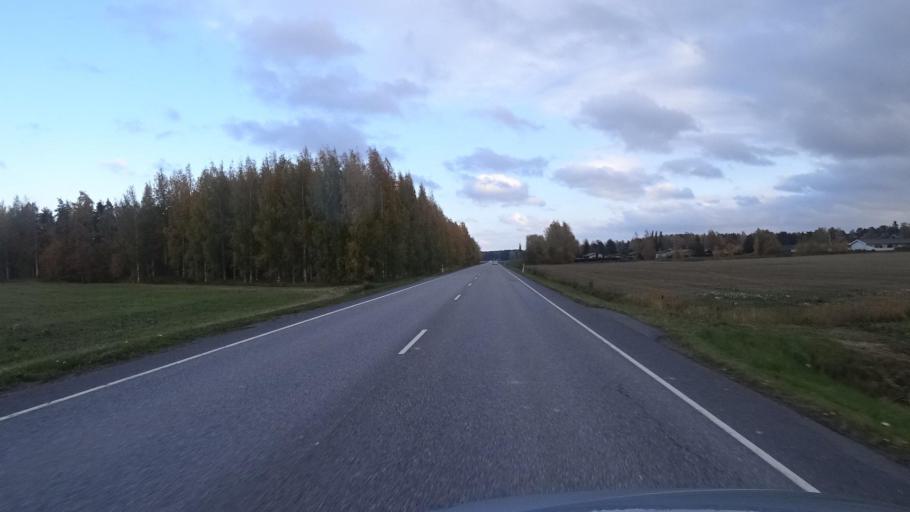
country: FI
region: Satakunta
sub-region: Rauma
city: Saekylae
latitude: 61.0443
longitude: 22.3675
